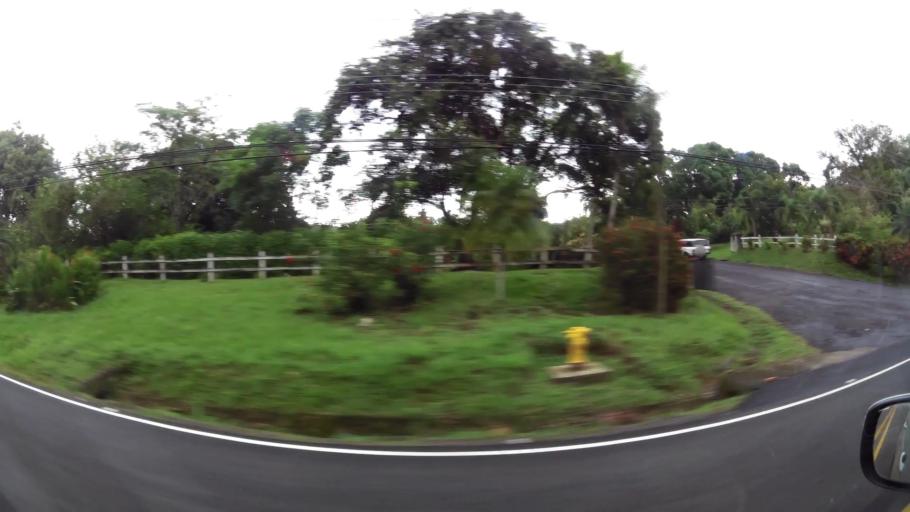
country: CR
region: Alajuela
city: Desamparados
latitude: 9.9394
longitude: -84.5343
